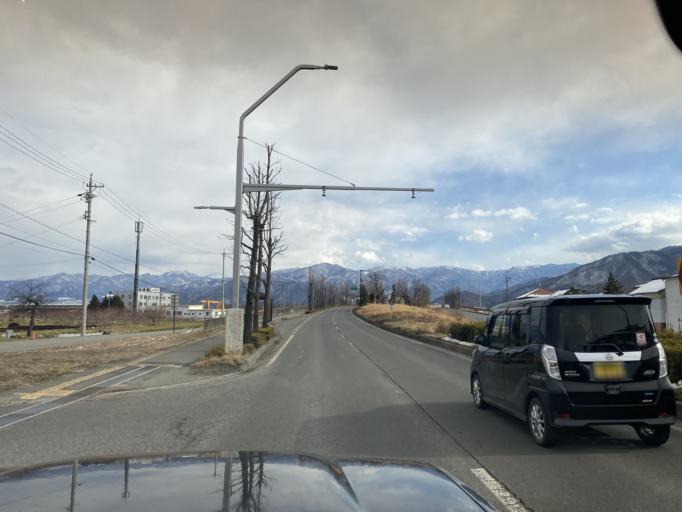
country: JP
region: Nagano
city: Suzaka
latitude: 36.6418
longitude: 138.2511
